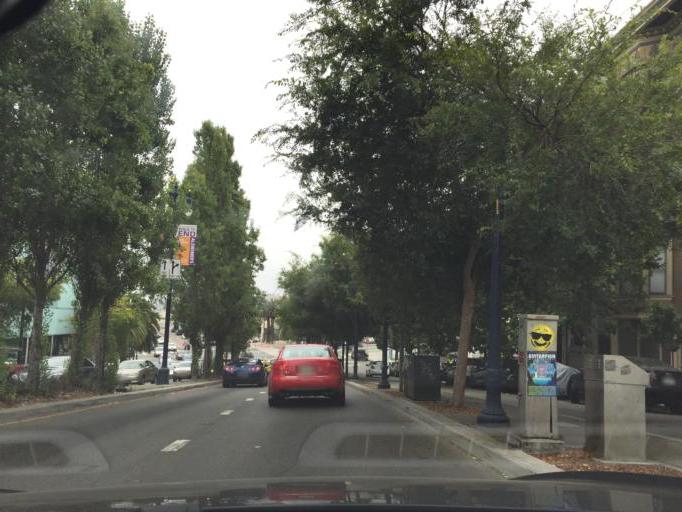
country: US
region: California
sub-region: San Francisco County
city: San Francisco
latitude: 37.7730
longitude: -122.4238
